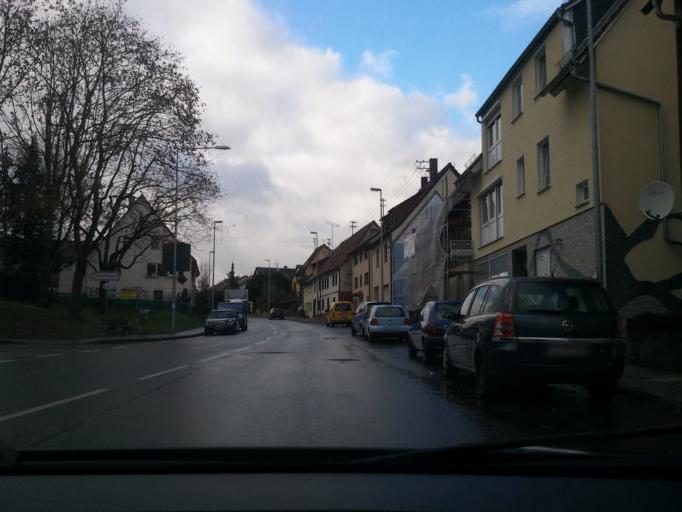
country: DE
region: Baden-Wuerttemberg
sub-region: Regierungsbezirk Stuttgart
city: Moglingen
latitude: 48.8871
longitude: 9.1260
